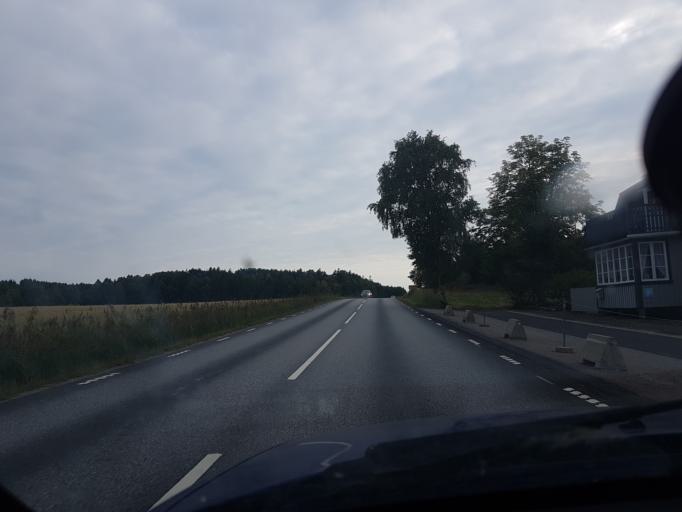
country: SE
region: Vaestra Goetaland
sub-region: Lysekils Kommun
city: Lysekil
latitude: 58.2892
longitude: 11.5502
